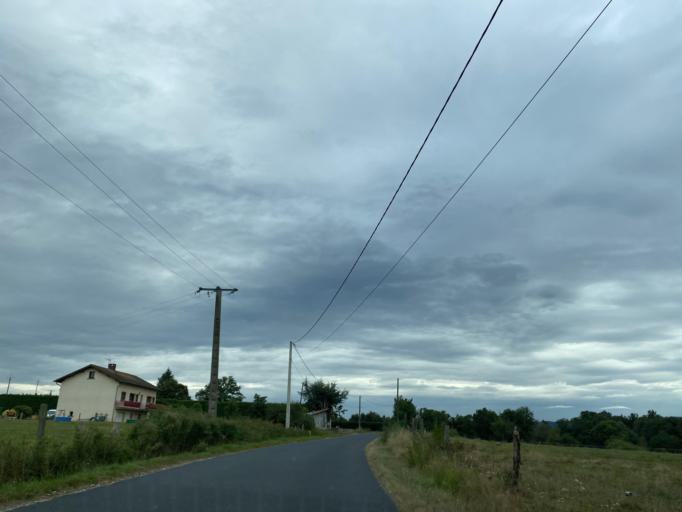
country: FR
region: Auvergne
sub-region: Departement du Puy-de-Dome
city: Marsac-en-Livradois
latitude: 45.4983
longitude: 3.7413
